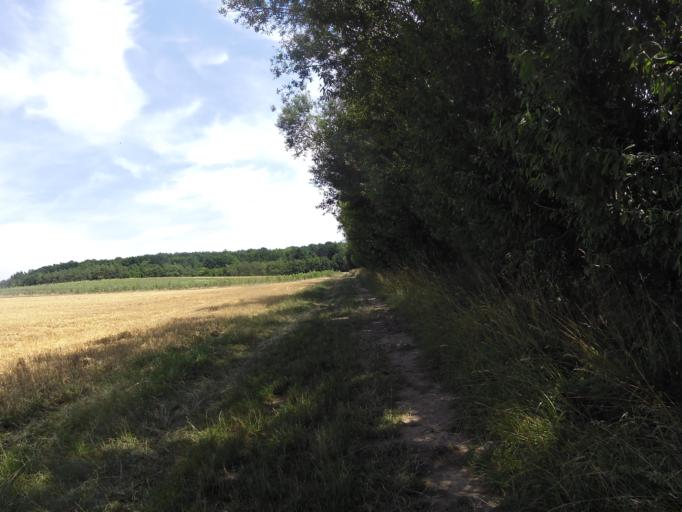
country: DE
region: Bavaria
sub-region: Regierungsbezirk Unterfranken
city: Estenfeld
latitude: 49.8078
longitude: 10.0075
